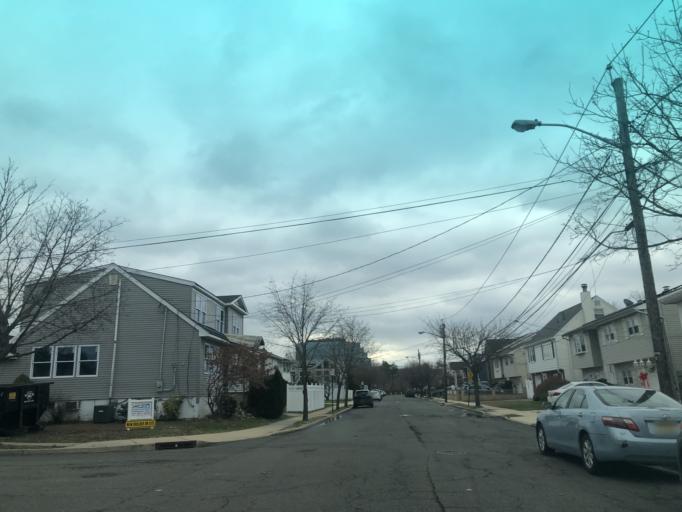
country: US
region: New Jersey
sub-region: Hudson County
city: Secaucus
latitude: 40.7937
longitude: -74.0548
